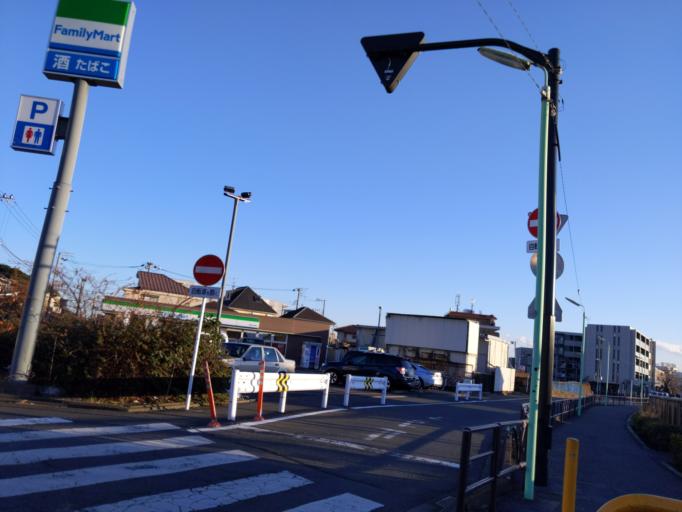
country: JP
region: Tokyo
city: Chofugaoka
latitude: 35.6242
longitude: 139.6132
